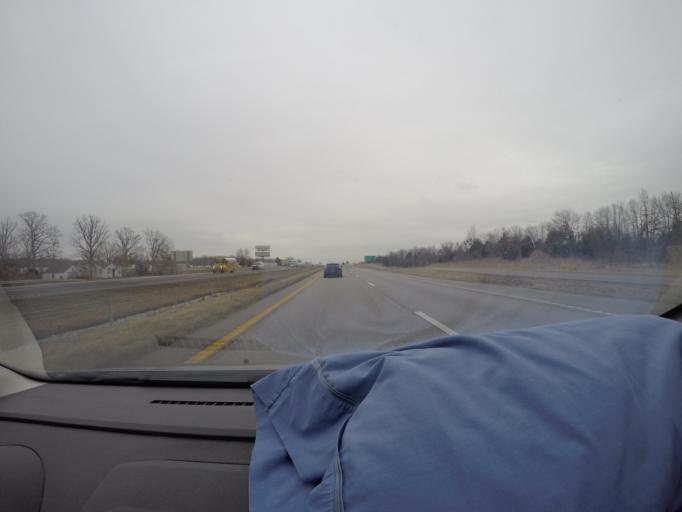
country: US
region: Missouri
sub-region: Warren County
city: Wright City
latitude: 38.8269
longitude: -91.0071
